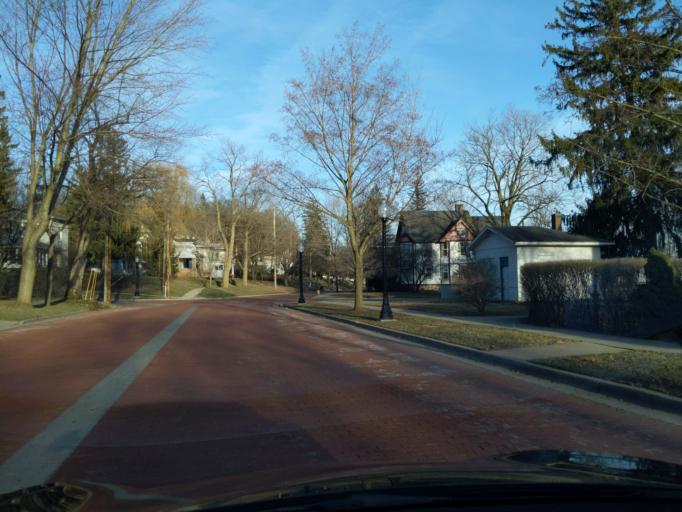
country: US
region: Michigan
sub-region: Ionia County
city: Ionia
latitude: 42.9834
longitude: -85.0552
